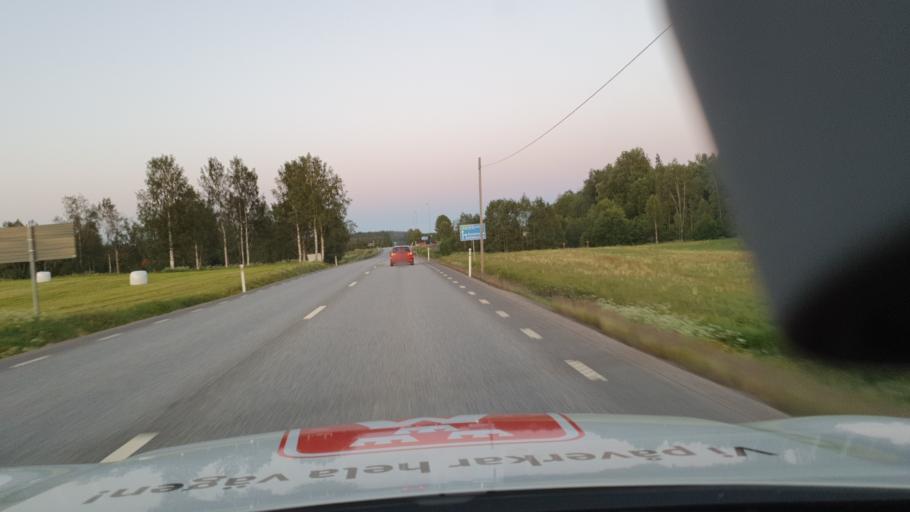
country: SE
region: Vaesterbotten
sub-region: Umea Kommun
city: Roback
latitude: 63.8775
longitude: 20.0564
